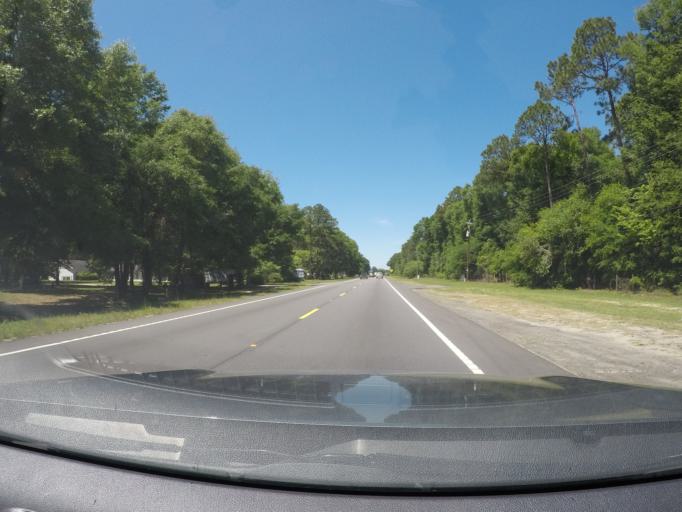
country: US
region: Georgia
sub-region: Chatham County
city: Bloomingdale
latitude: 32.1938
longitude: -81.4274
